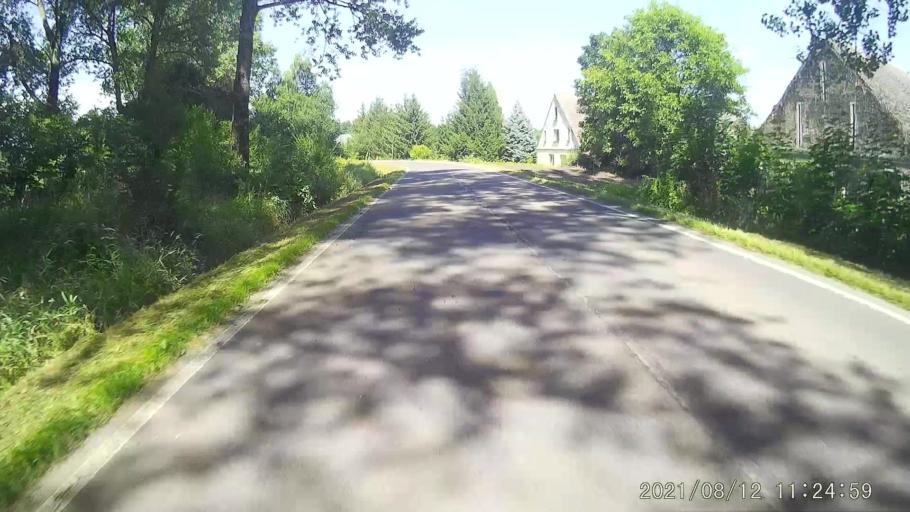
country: PL
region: Lower Silesian Voivodeship
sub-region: Powiat klodzki
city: Bystrzyca Klodzka
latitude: 50.2889
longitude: 16.6756
